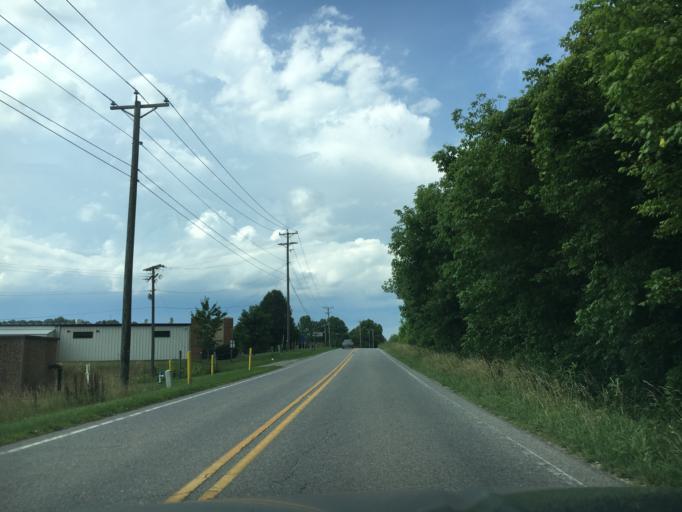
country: US
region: Virginia
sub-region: Roanoke County
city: Cave Spring
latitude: 37.1965
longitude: -79.9995
